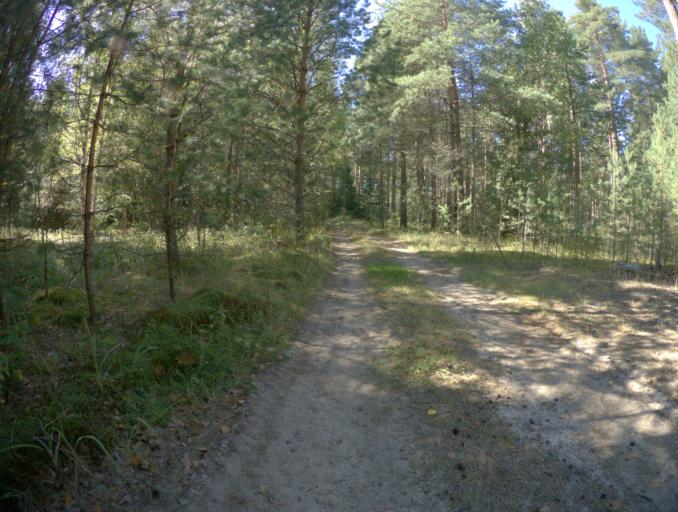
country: RU
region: Vladimir
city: Dobryatino
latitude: 55.7313
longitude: 41.4912
